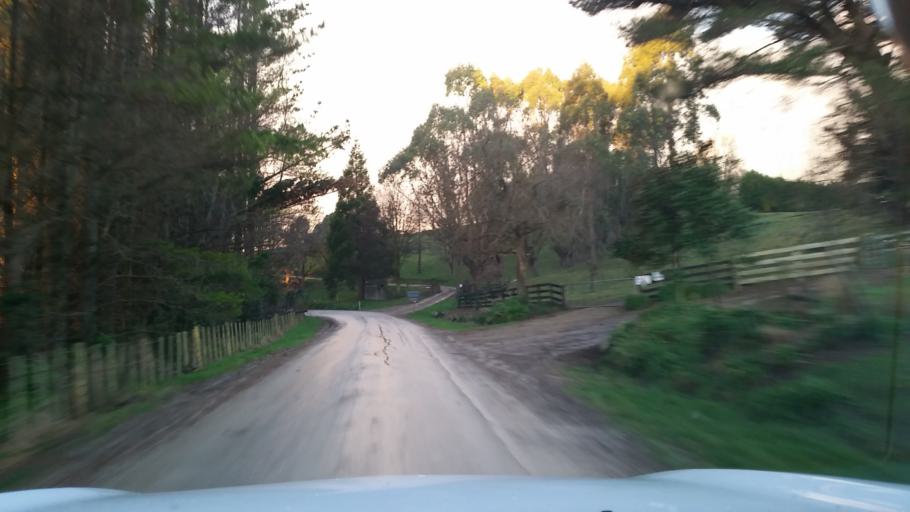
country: NZ
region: Manawatu-Wanganui
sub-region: Wanganui District
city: Wanganui
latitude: -39.7736
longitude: 174.8635
